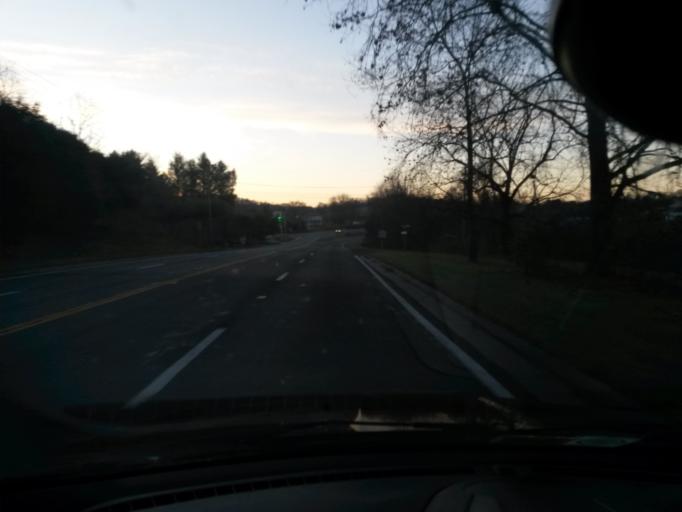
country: US
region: Virginia
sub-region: Botetourt County
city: Fincastle
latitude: 37.4939
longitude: -79.8783
